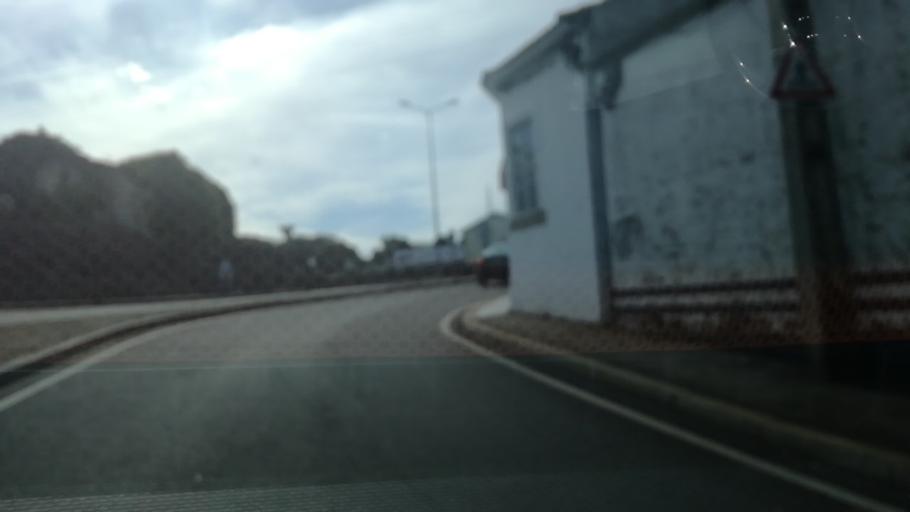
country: PT
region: Porto
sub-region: Valongo
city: Ermesinde
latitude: 41.2268
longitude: -8.5658
